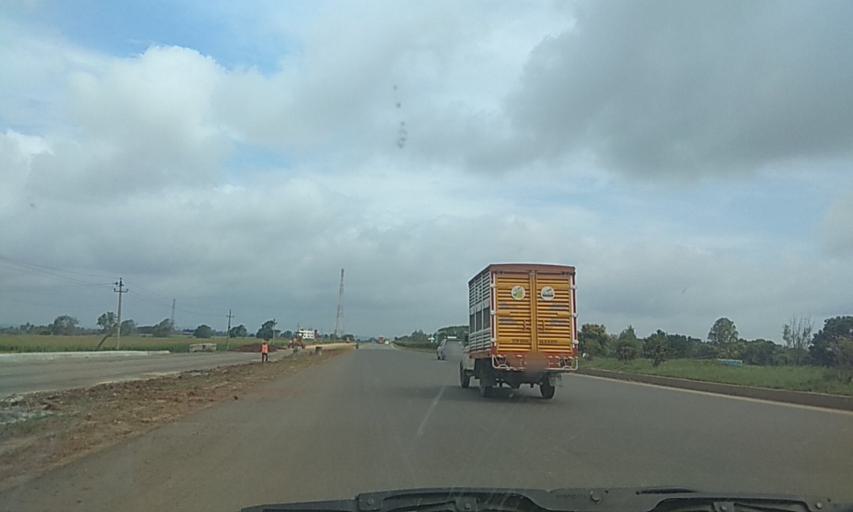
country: IN
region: Karnataka
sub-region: Dharwad
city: Kundgol
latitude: 15.1805
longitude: 75.1385
